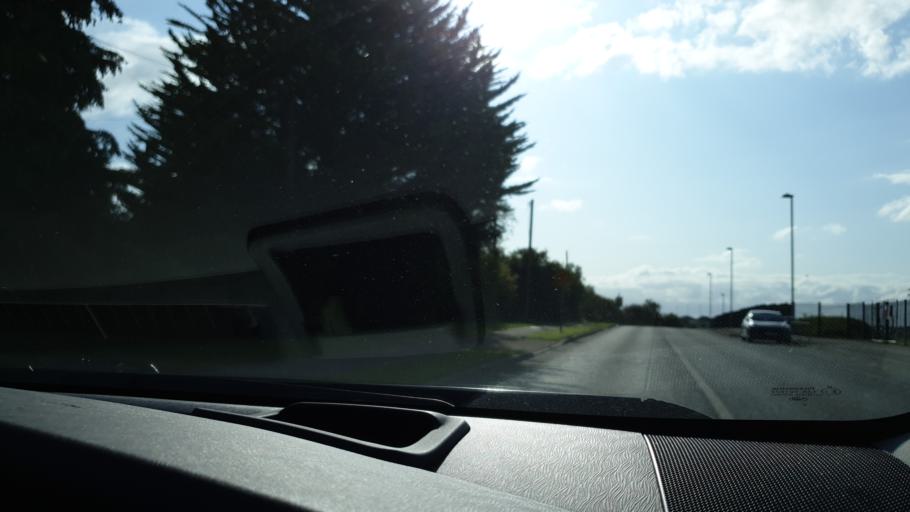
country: IE
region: Leinster
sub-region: An Mhi
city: Ashbourne
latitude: 53.5098
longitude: -6.4010
